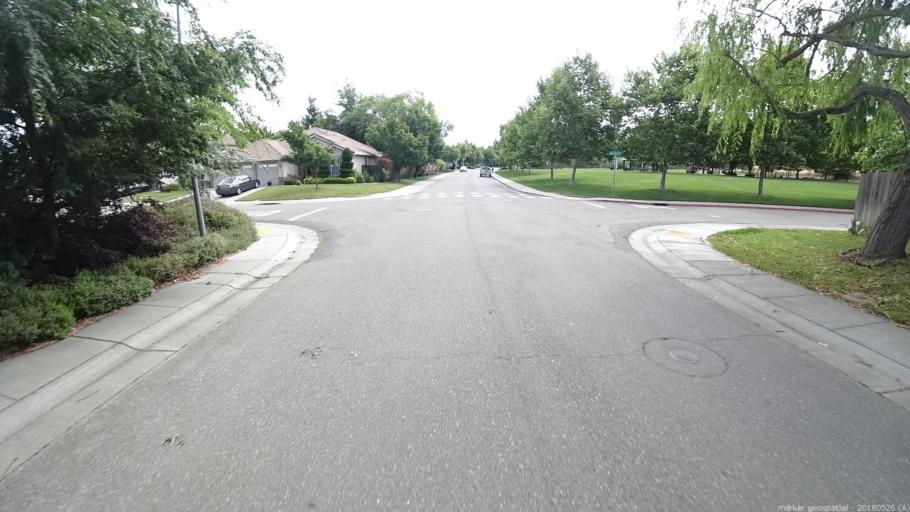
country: US
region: California
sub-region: Yolo County
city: West Sacramento
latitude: 38.6055
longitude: -121.5370
